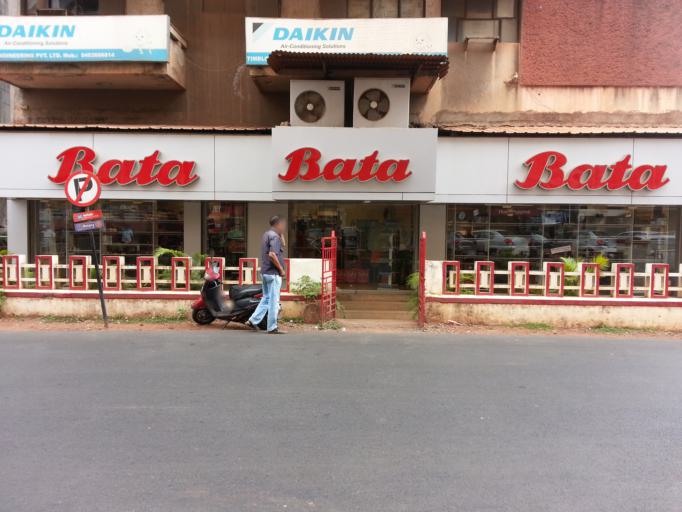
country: IN
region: Goa
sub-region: South Goa
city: Madgaon
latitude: 15.2728
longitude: 73.9614
